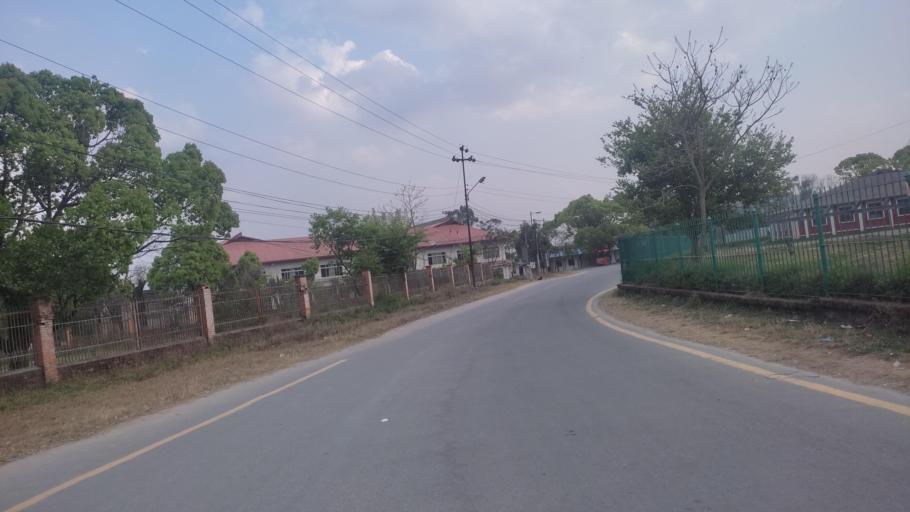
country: NP
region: Central Region
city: Kirtipur
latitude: 27.6825
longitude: 85.2840
